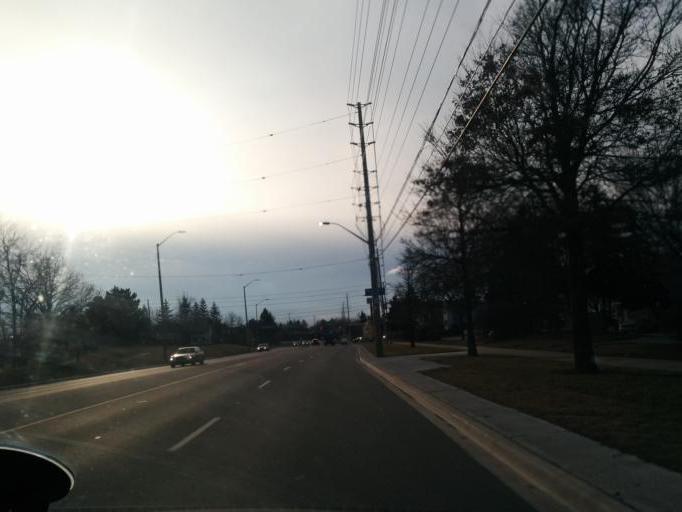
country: CA
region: Ontario
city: Mississauga
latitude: 43.5437
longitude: -79.6893
